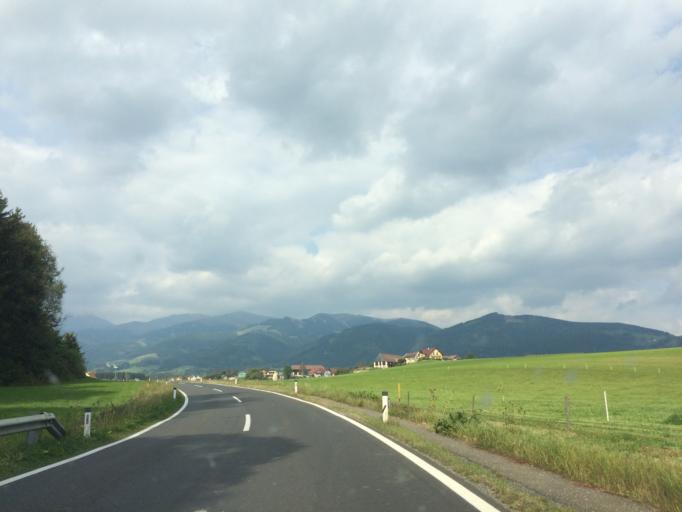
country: AT
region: Styria
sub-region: Politischer Bezirk Murtal
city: Kobenz
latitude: 47.2619
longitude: 14.8325
